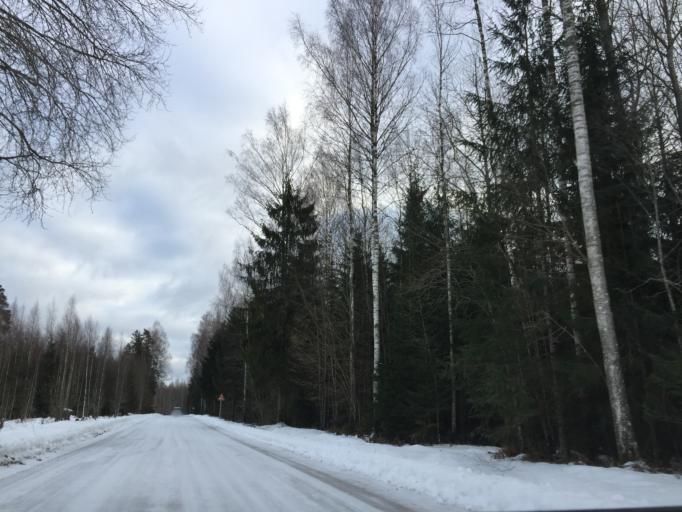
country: LV
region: Lielvarde
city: Lielvarde
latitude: 56.5820
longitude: 24.7501
